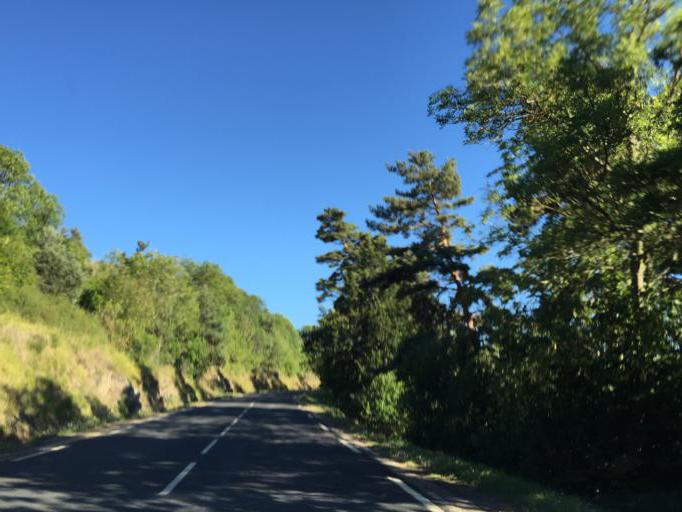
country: FR
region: Auvergne
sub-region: Departement de la Haute-Loire
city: Bains
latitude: 44.9940
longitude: 3.6922
